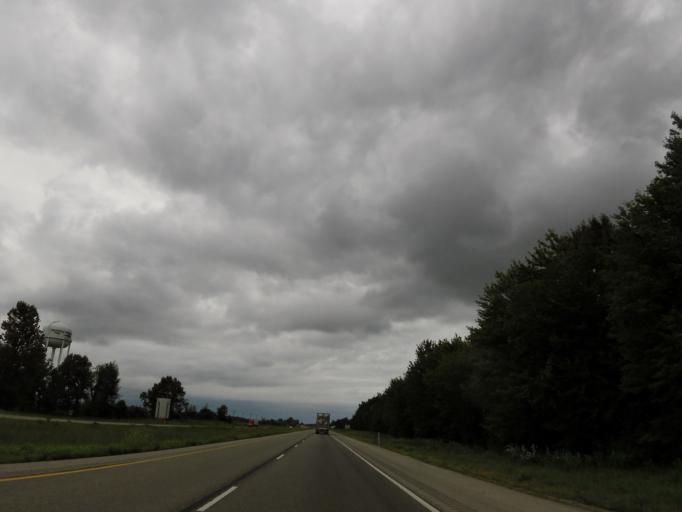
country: US
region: Illinois
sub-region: Massac County
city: Metropolis
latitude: 37.1711
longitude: -88.6824
